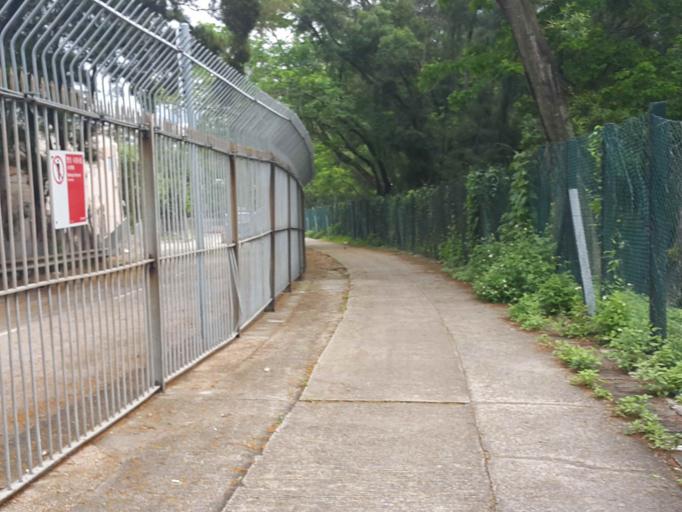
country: HK
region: Wong Tai Sin
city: Wong Tai Sin
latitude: 22.3395
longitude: 114.1740
